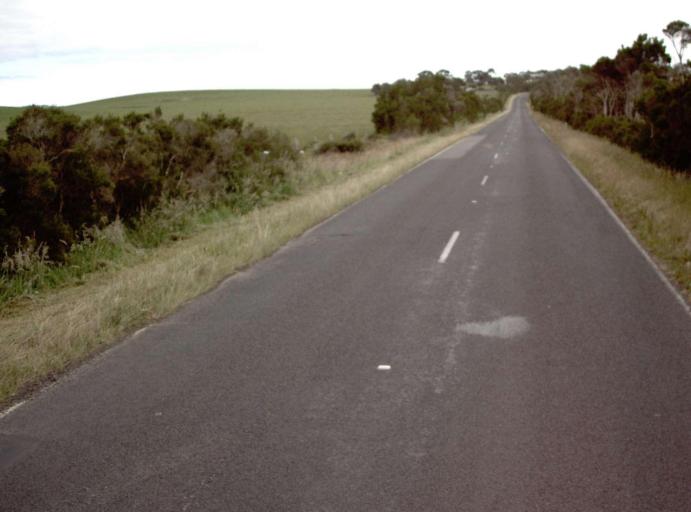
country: AU
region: Victoria
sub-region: Bass Coast
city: North Wonthaggi
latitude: -38.5665
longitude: 145.6328
